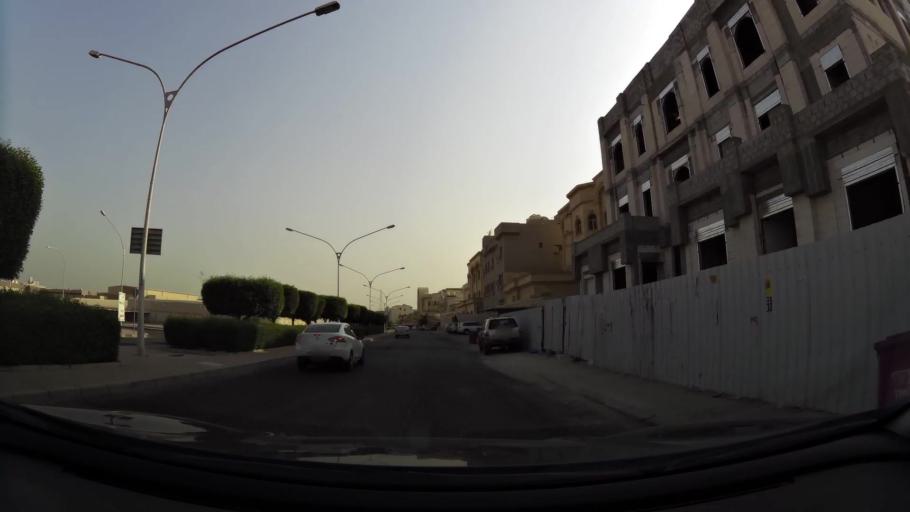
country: KW
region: Al Ahmadi
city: Al Manqaf
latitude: 29.1015
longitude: 48.1049
